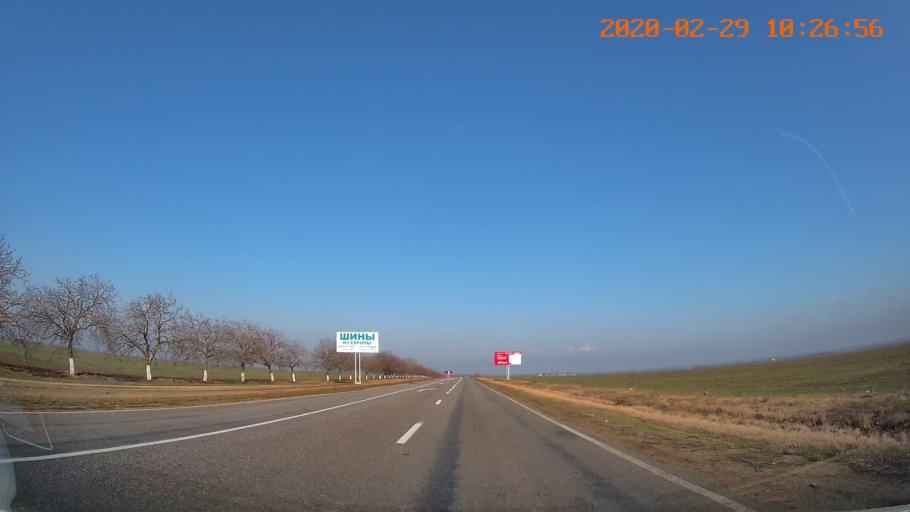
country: MD
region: Telenesti
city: Tiraspolul Nou
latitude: 46.8894
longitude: 29.6007
